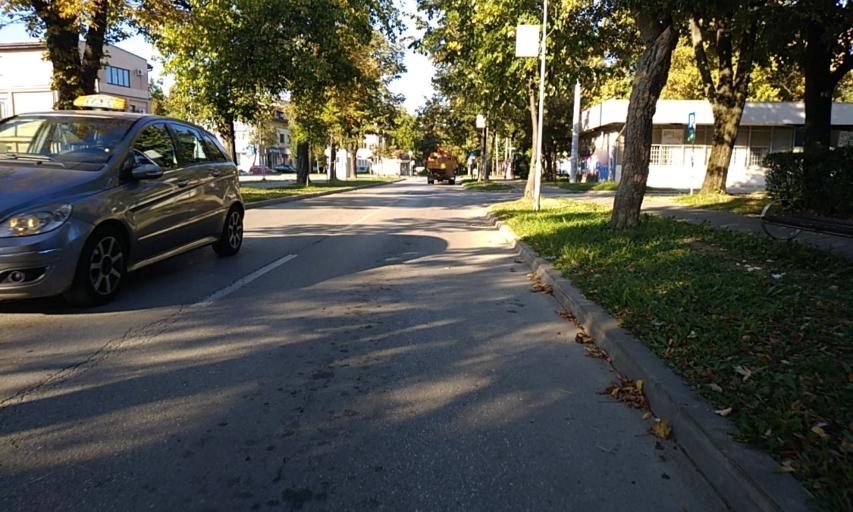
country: BA
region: Republika Srpska
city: Banja Luka
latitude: 44.7755
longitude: 17.1878
